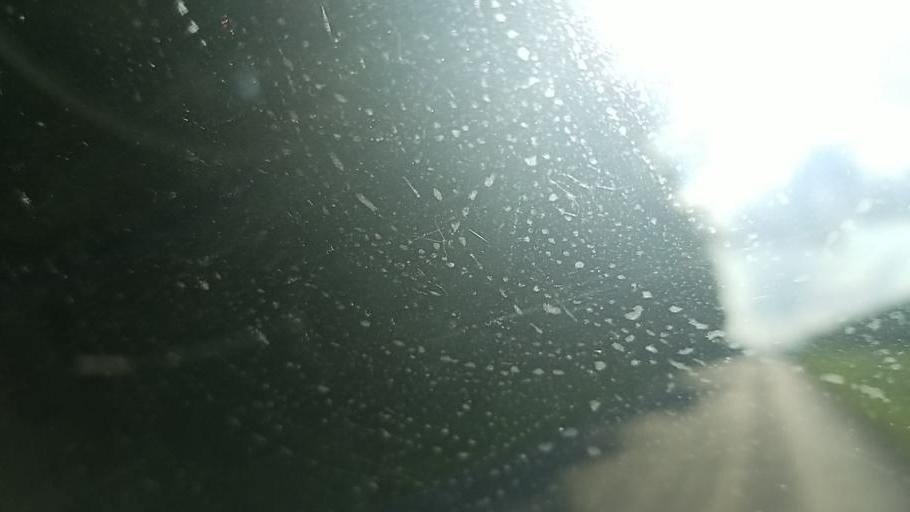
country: US
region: Ohio
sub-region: Wayne County
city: West Salem
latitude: 40.8727
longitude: -82.0807
